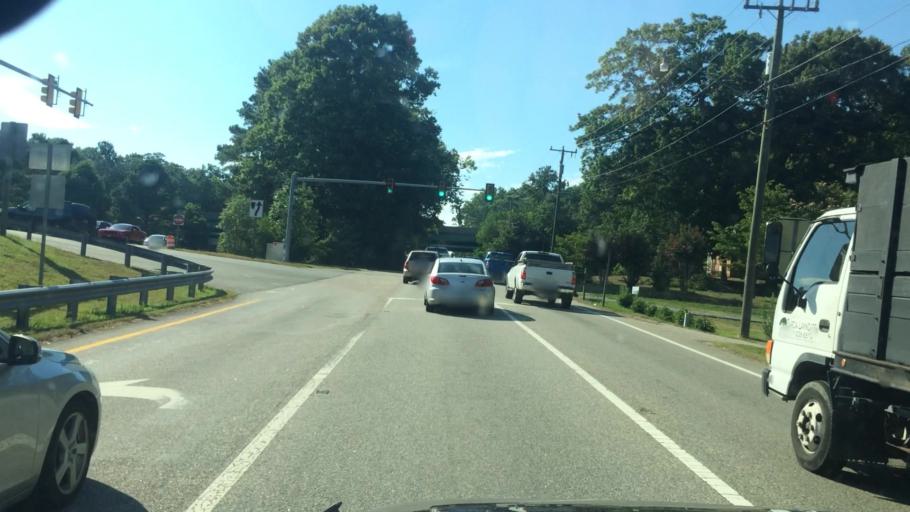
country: US
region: Virginia
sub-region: James City County
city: Williamsburg
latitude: 37.3356
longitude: -76.7489
